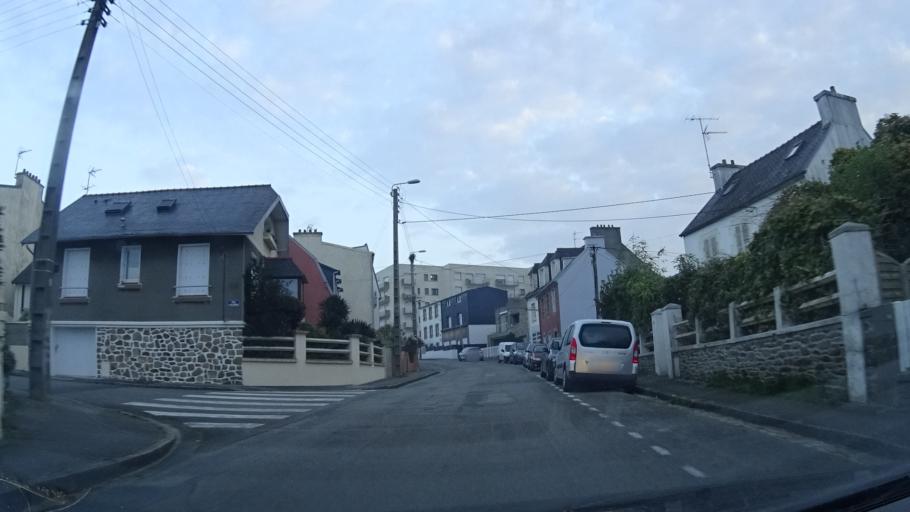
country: FR
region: Brittany
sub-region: Departement du Finistere
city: Brest
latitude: 48.3970
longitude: -4.4585
